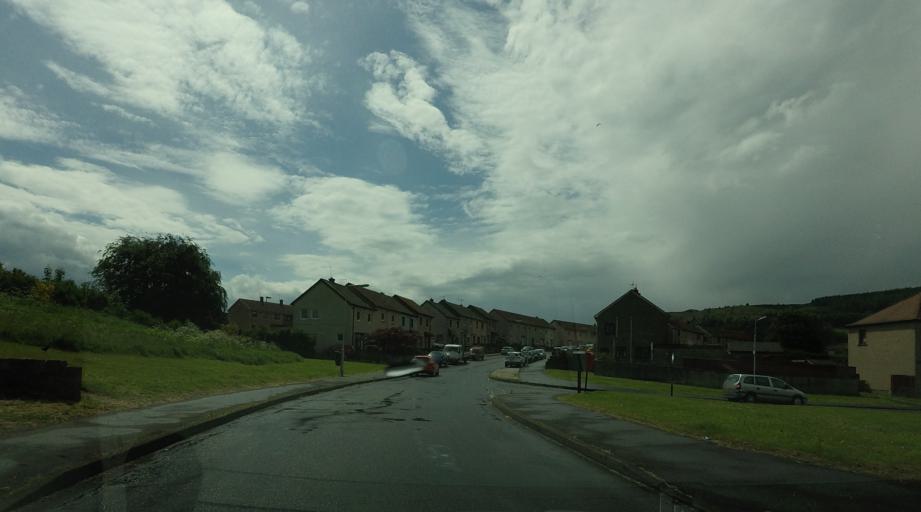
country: GB
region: Scotland
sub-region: Fife
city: Ballingry
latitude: 56.1619
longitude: -3.3256
